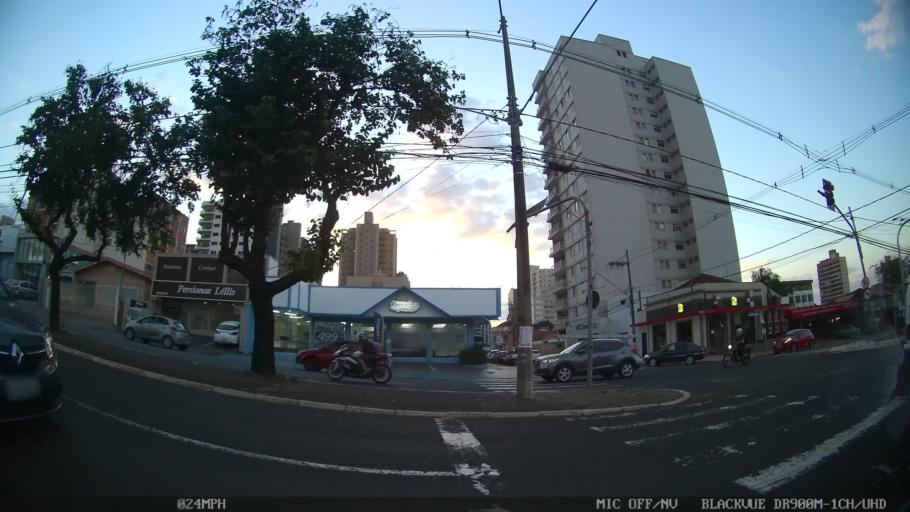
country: BR
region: Sao Paulo
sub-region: Ribeirao Preto
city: Ribeirao Preto
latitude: -21.1851
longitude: -47.8045
